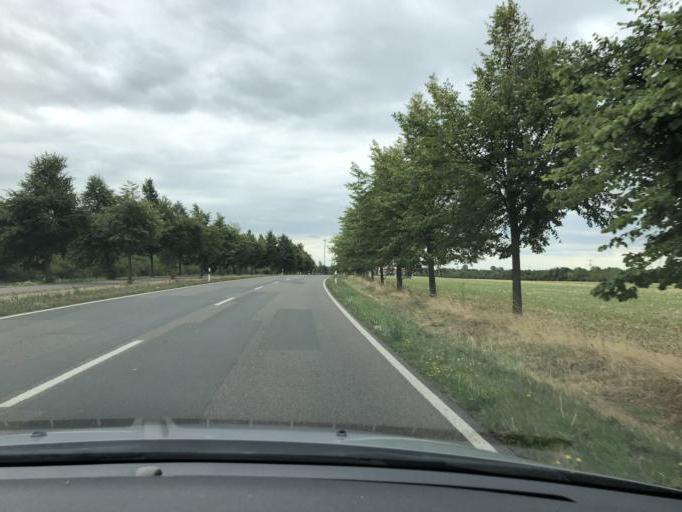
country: DE
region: Saxony
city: Rackwitz
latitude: 51.4177
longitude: 12.4067
